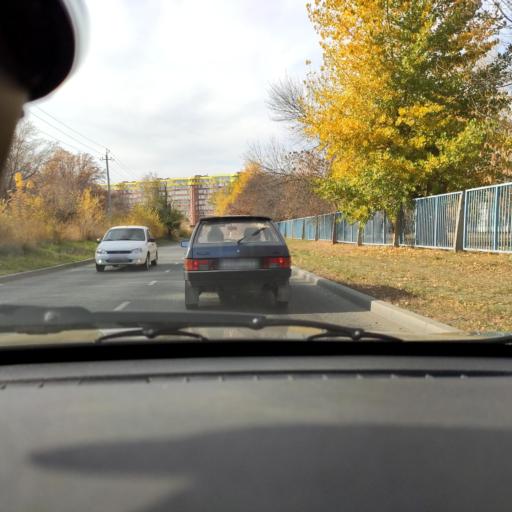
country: RU
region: Samara
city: Tol'yatti
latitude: 53.5195
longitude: 49.3203
